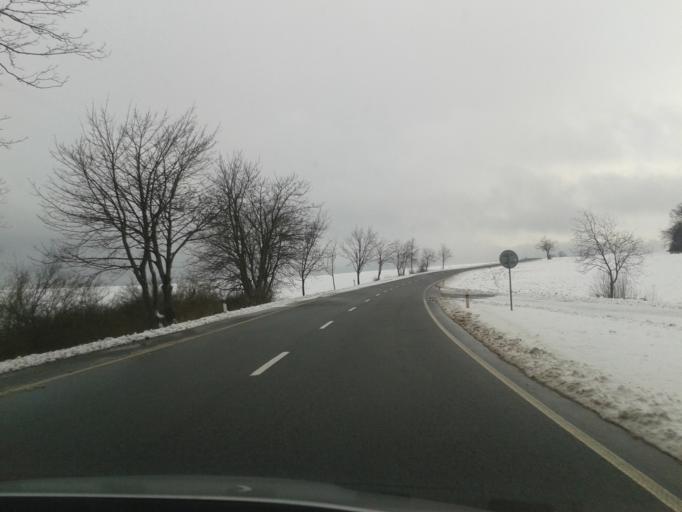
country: CZ
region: Olomoucky
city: Protivanov
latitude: 49.4707
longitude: 16.7799
